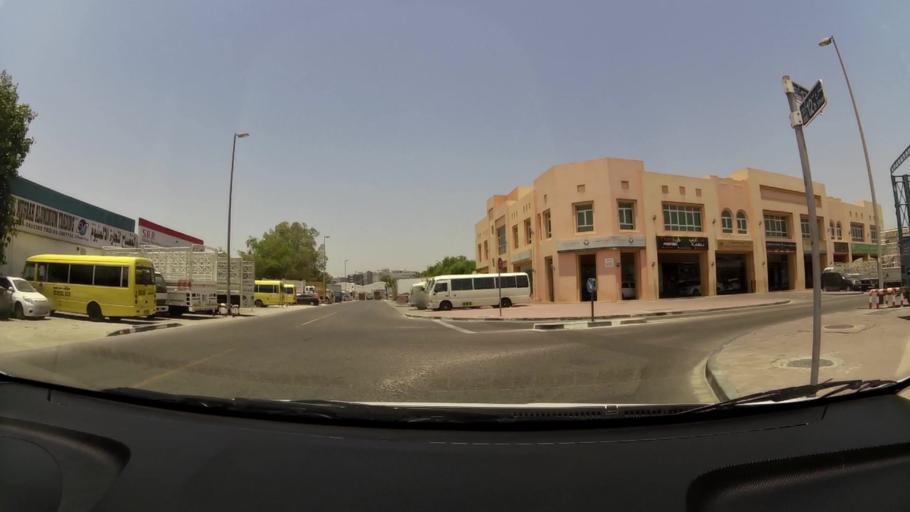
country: AE
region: Ash Shariqah
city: Sharjah
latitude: 25.2675
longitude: 55.3361
